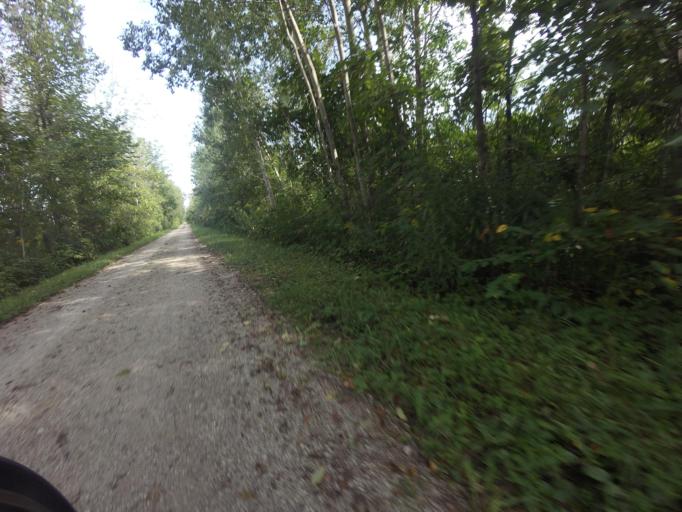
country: CA
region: Ontario
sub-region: Wellington County
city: Guelph
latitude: 43.5827
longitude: -80.4091
